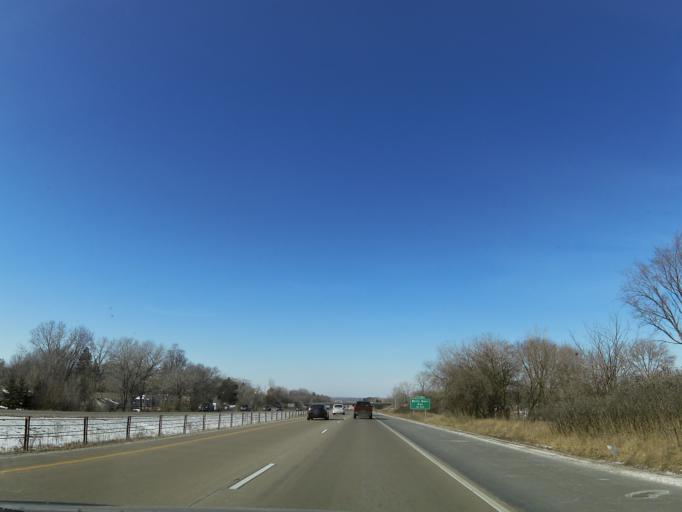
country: US
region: Minnesota
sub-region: Ramsey County
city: North Saint Paul
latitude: 45.0360
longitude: -92.9982
